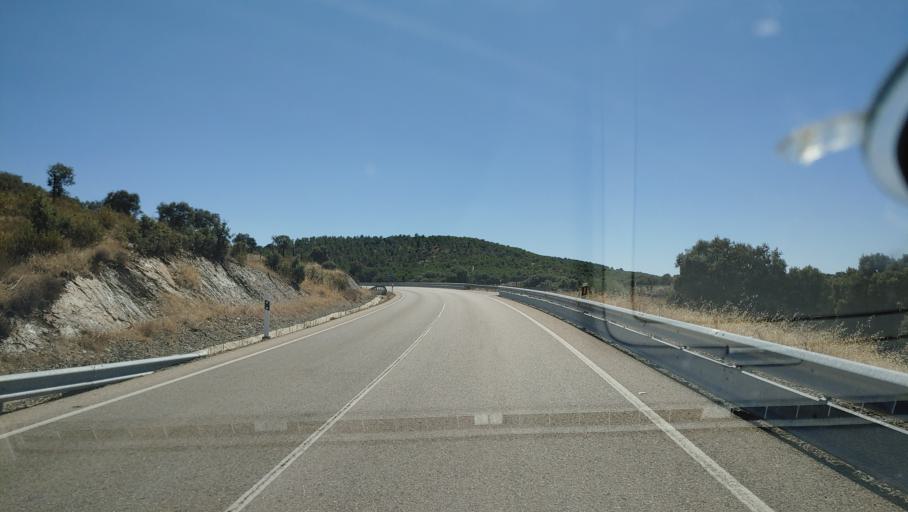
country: ES
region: Andalusia
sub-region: Provincia de Jaen
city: Genave
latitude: 38.4913
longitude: -2.7667
